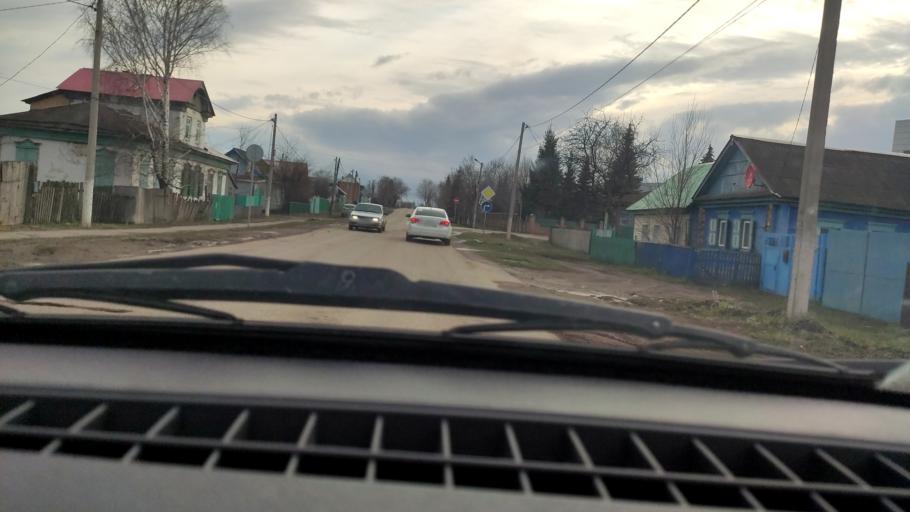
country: RU
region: Bashkortostan
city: Davlekanovo
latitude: 54.2111
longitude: 55.0288
